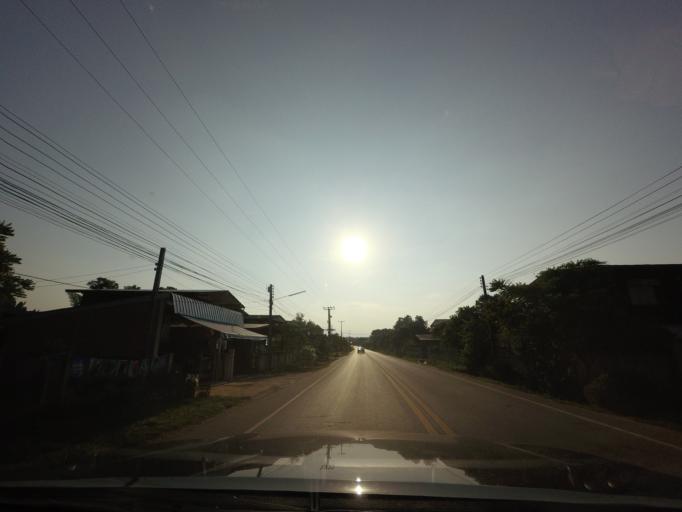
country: TH
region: Nan
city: Na Noi
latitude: 18.3351
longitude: 100.7512
